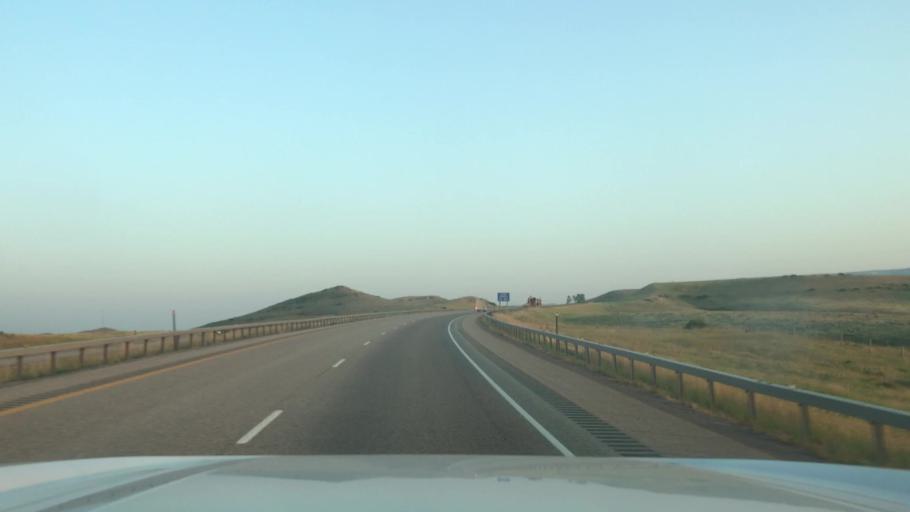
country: US
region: Wyoming
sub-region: Sheridan County
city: Sheridan
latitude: 44.7112
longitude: -106.9119
